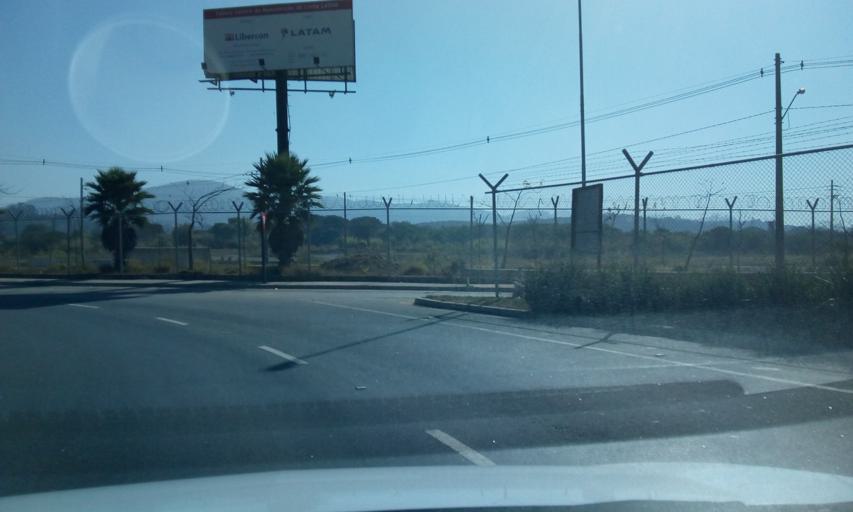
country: BR
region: Sao Paulo
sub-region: Guarulhos
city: Guarulhos
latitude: -23.4205
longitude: -46.4743
